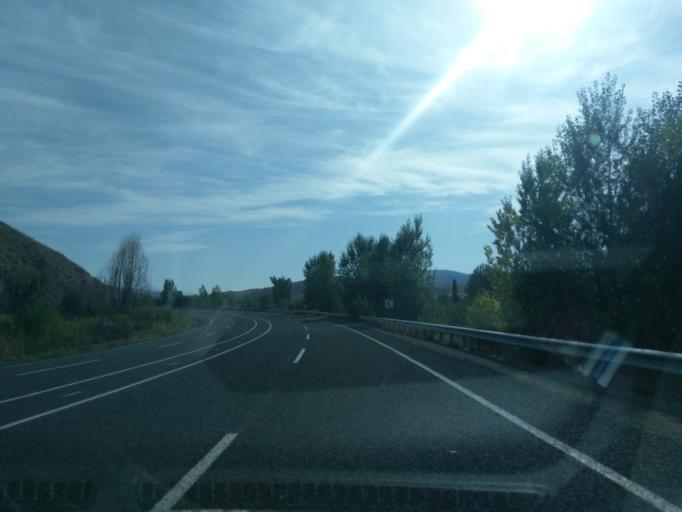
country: TR
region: Sivas
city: Zara
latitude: 39.8488
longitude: 37.8452
